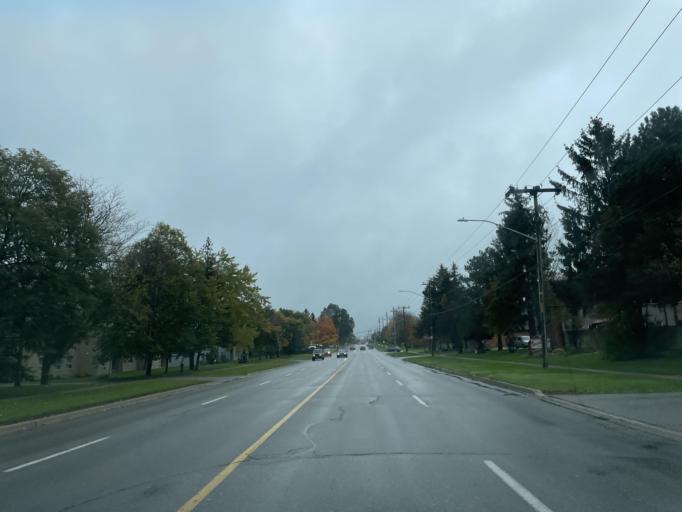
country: CA
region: Ontario
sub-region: Wellington County
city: Guelph
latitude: 43.5366
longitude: -80.2757
